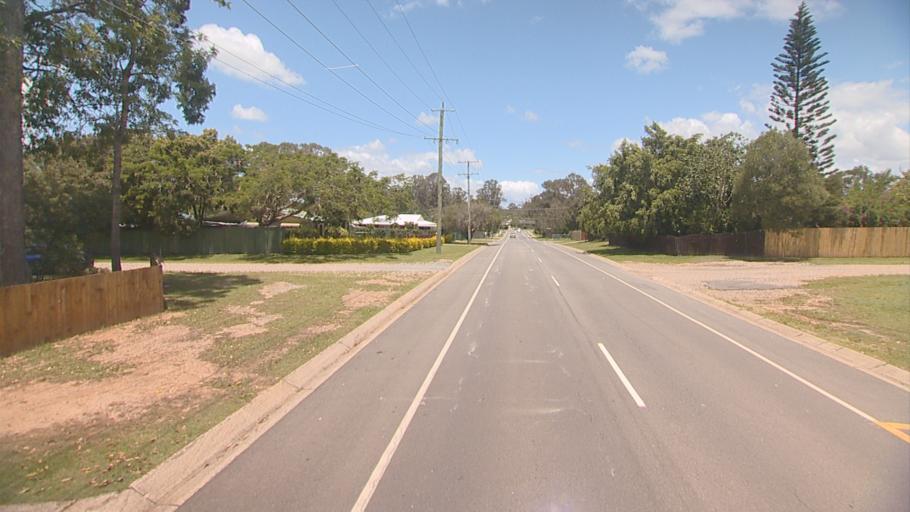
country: AU
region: Queensland
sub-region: Logan
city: Beenleigh
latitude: -27.6990
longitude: 153.2055
